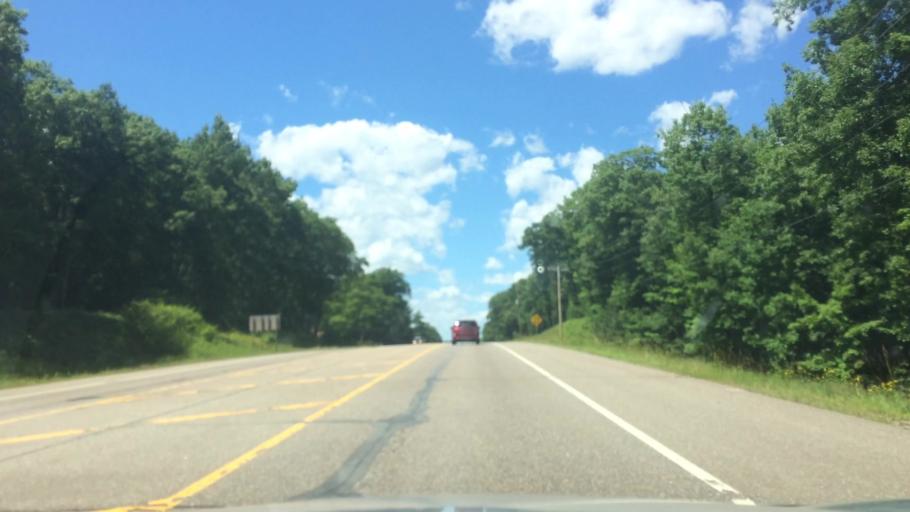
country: US
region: Wisconsin
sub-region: Vilas County
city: Lac du Flambeau
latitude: 45.7930
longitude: -89.7142
